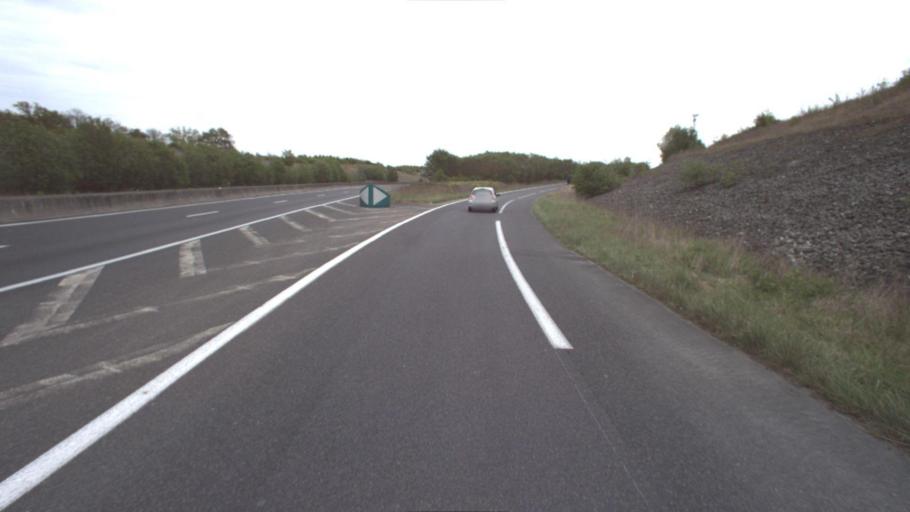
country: FR
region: Ile-de-France
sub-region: Departement de Seine-et-Marne
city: Mareuil-les-Meaux
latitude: 48.9169
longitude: 2.8667
